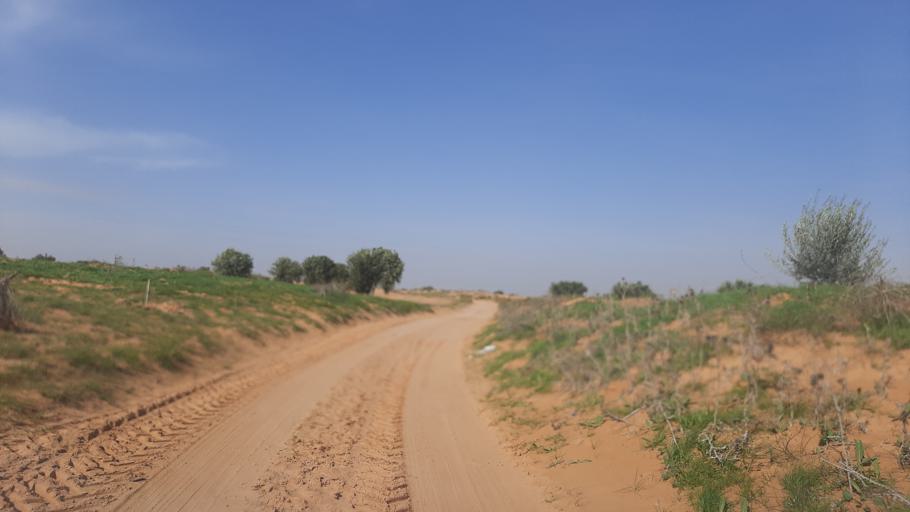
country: TN
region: Madanin
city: Zarzis
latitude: 33.4356
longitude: 10.8084
